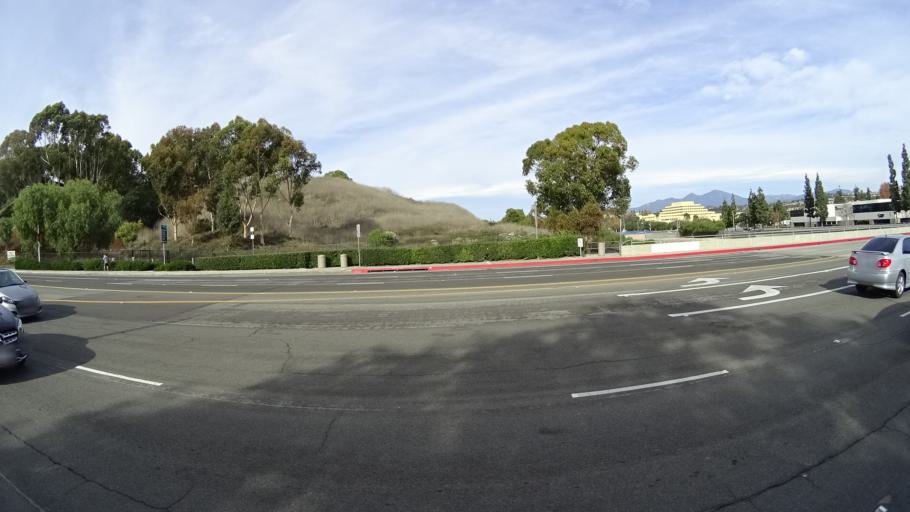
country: US
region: California
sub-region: Orange County
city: Aliso Viejo
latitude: 33.5556
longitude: -117.7189
